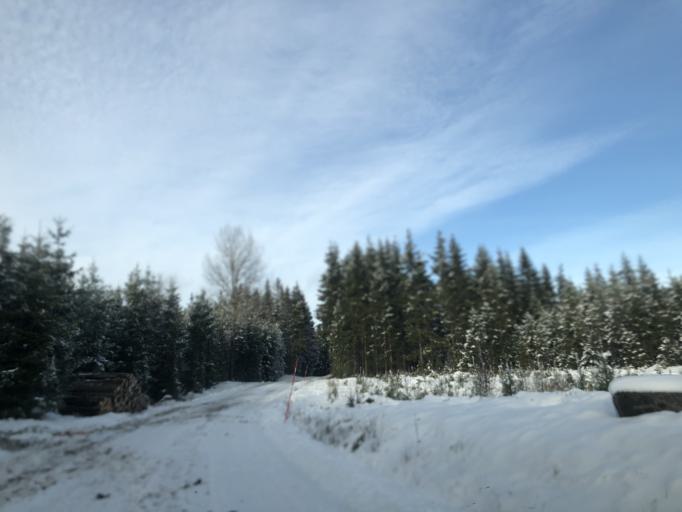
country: SE
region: Vaestra Goetaland
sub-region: Ulricehamns Kommun
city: Ulricehamn
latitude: 57.7595
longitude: 13.5177
